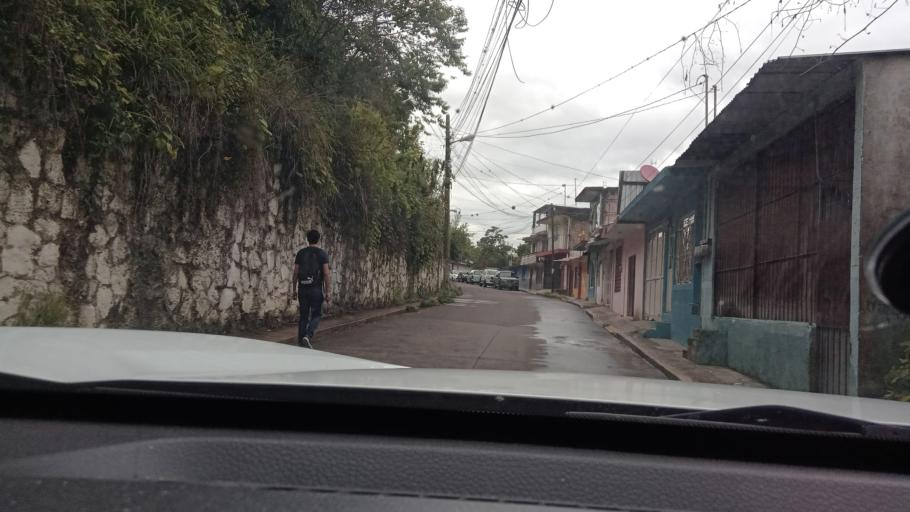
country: MX
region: Veracruz
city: Coatepec
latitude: 19.4467
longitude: -96.9609
